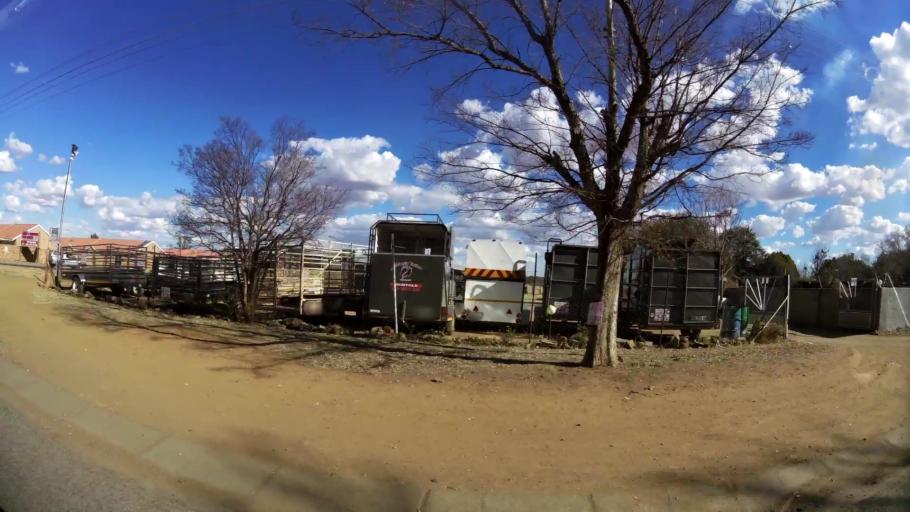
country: ZA
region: North-West
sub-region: Dr Kenneth Kaunda District Municipality
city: Klerksdorp
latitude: -26.8463
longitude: 26.6532
